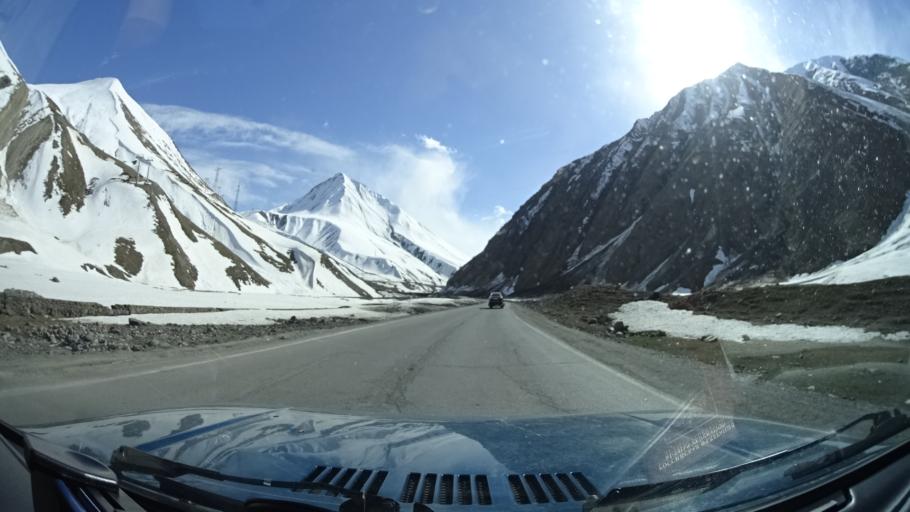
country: GE
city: Gudauri
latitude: 42.5509
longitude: 44.4951
